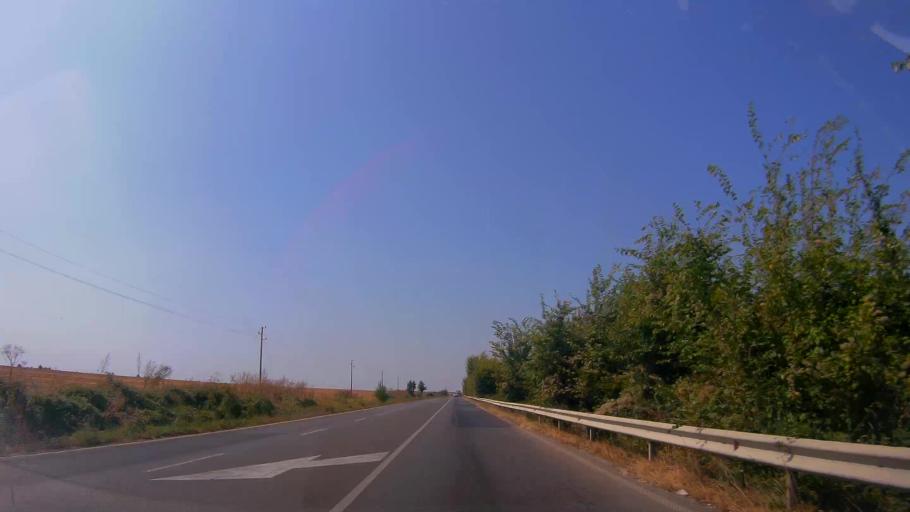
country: BG
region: Ruse
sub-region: Obshtina Vetovo
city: Senovo
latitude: 43.5620
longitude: 26.3506
